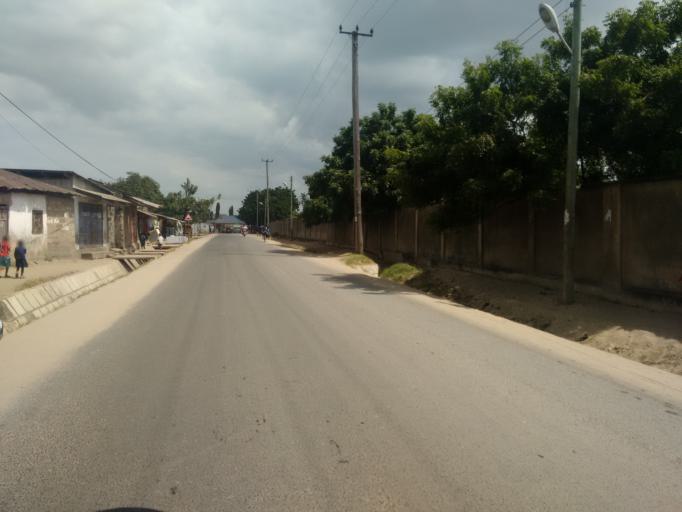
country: TZ
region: Dar es Salaam
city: Dar es Salaam
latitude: -6.8561
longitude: 39.2478
